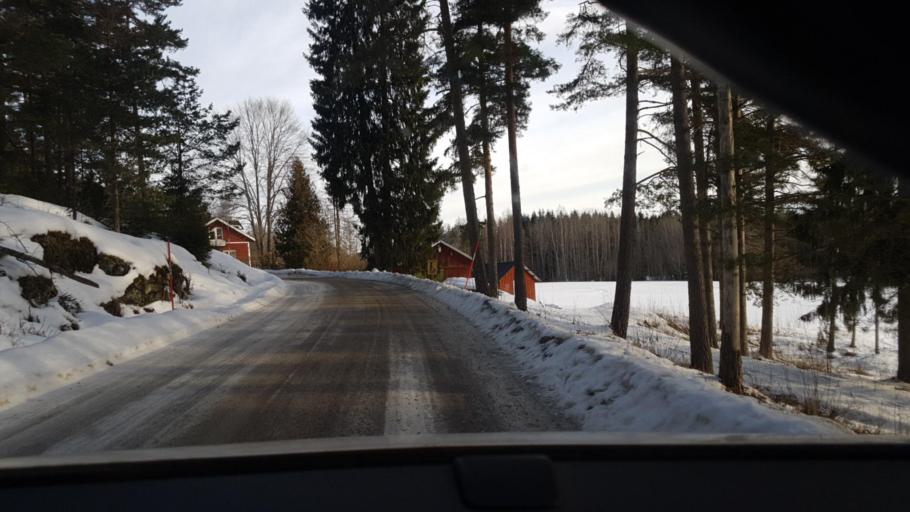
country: SE
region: Vaermland
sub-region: Eda Kommun
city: Amotfors
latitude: 59.7328
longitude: 12.2782
